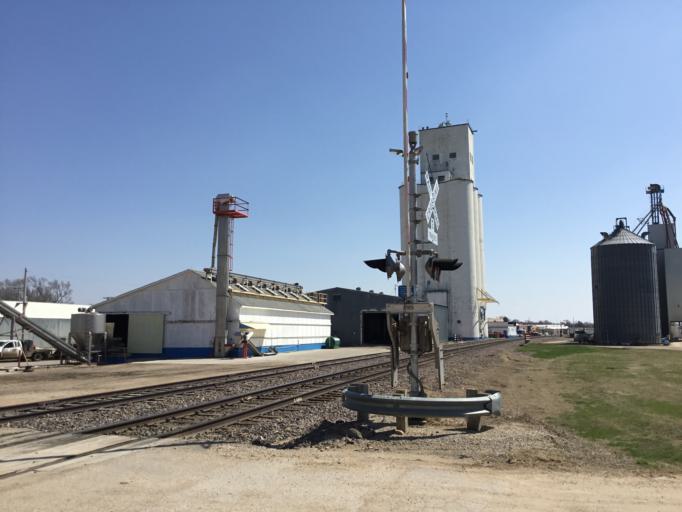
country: US
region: Kansas
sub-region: Ellsworth County
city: Ellsworth
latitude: 38.7303
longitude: -98.2352
